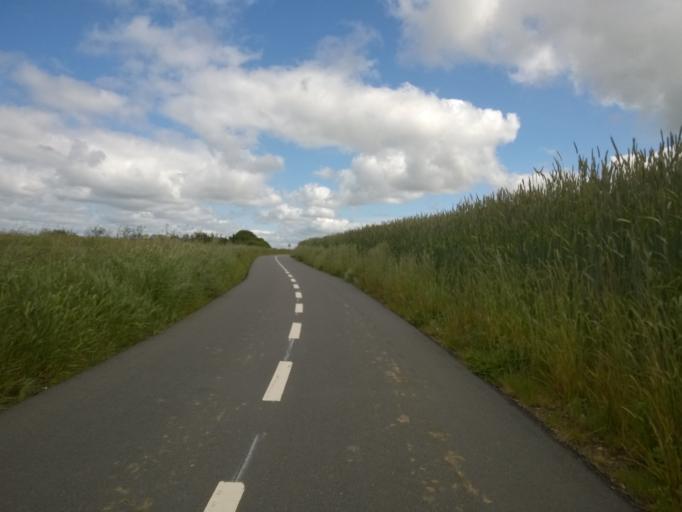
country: DK
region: Central Jutland
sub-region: Holstebro Kommune
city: Vinderup
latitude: 56.4747
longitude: 8.8121
